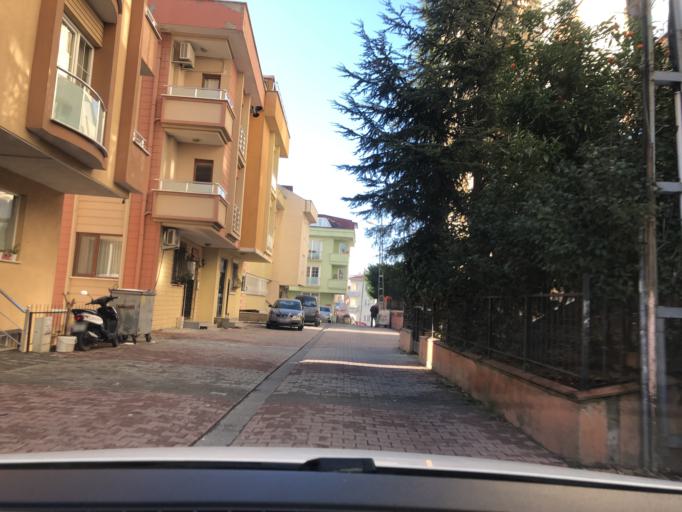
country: TR
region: Istanbul
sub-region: Atasehir
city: Atasehir
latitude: 40.9727
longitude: 29.1231
